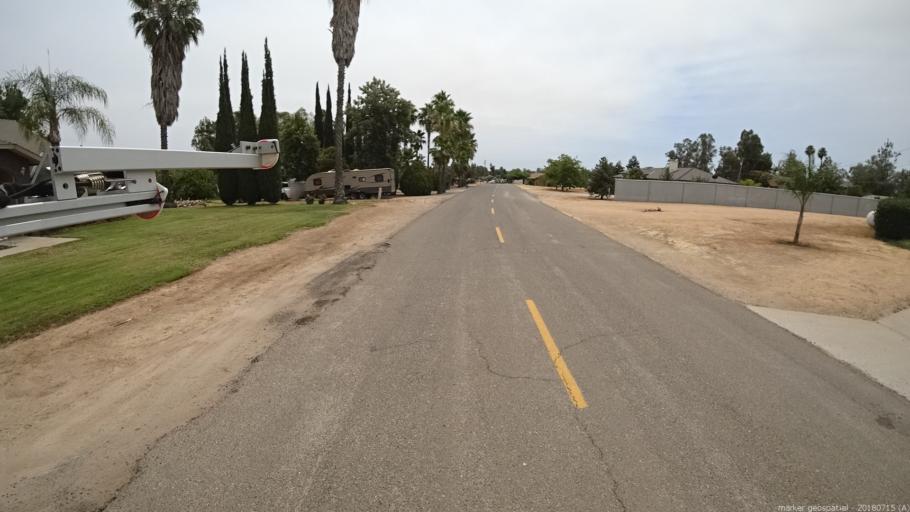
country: US
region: California
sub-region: Madera County
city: Madera Acres
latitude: 37.0054
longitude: -120.0886
